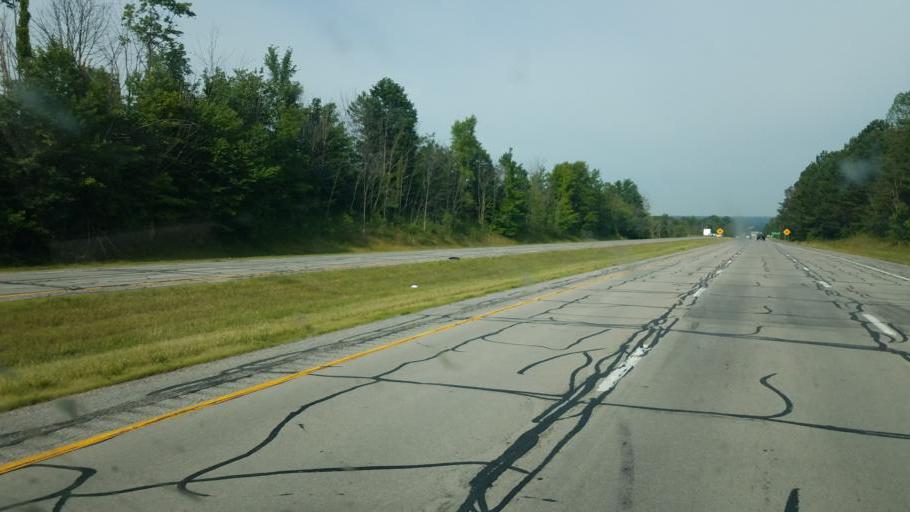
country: US
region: Ohio
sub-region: Medina County
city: Lodi
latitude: 41.0467
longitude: -81.9982
